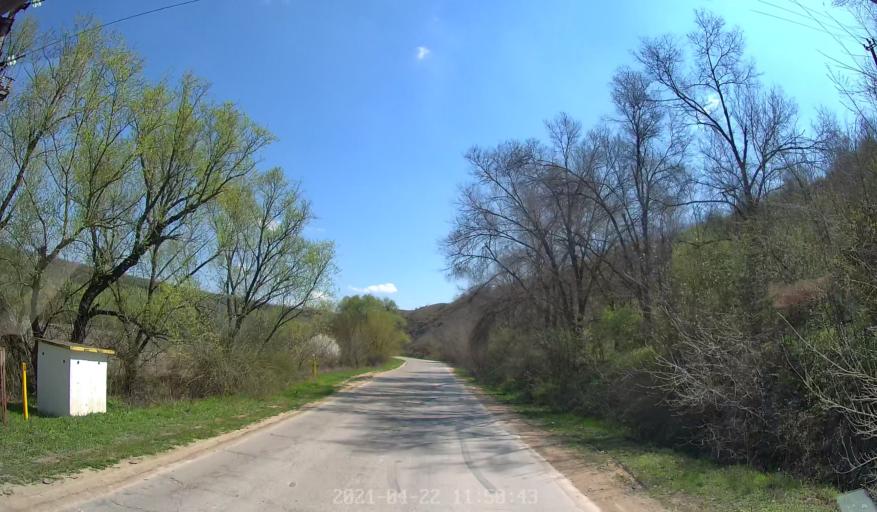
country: MD
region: Chisinau
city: Ciorescu
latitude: 47.1365
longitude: 28.9016
